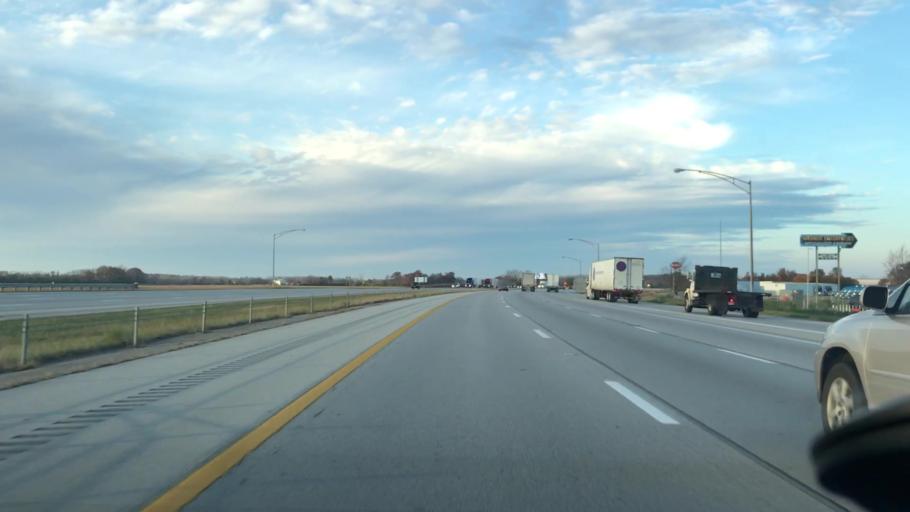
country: US
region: Ohio
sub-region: Clark County
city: Springfield
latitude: 39.8944
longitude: -83.7262
